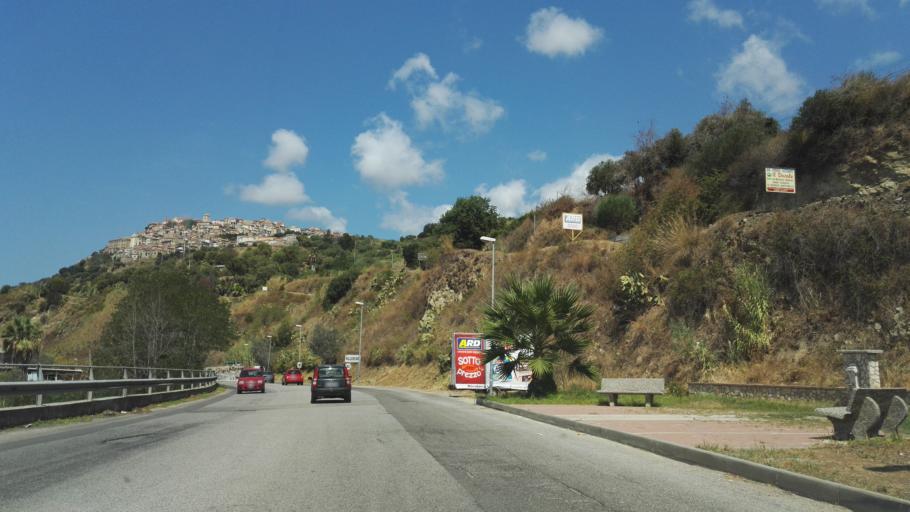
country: IT
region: Calabria
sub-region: Provincia di Vibo-Valentia
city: Nicotera
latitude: 38.5446
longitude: 15.9477
